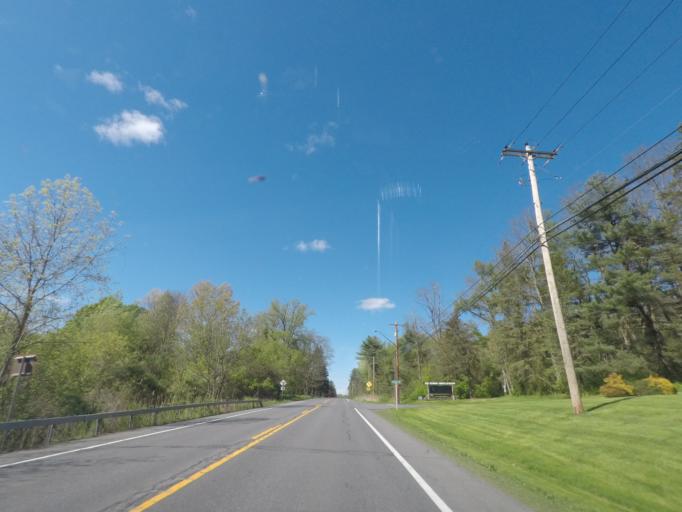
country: US
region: New York
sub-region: Albany County
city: Delmar
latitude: 42.5640
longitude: -73.8064
